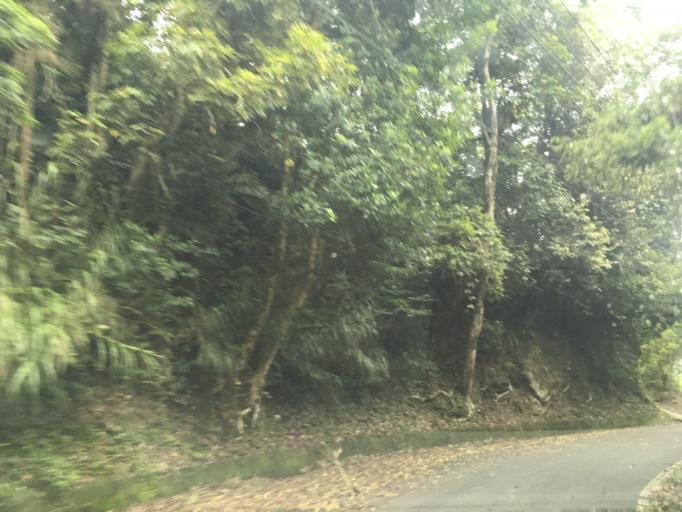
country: TW
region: Taiwan
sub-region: Yunlin
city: Douliu
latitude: 23.5676
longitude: 120.6301
